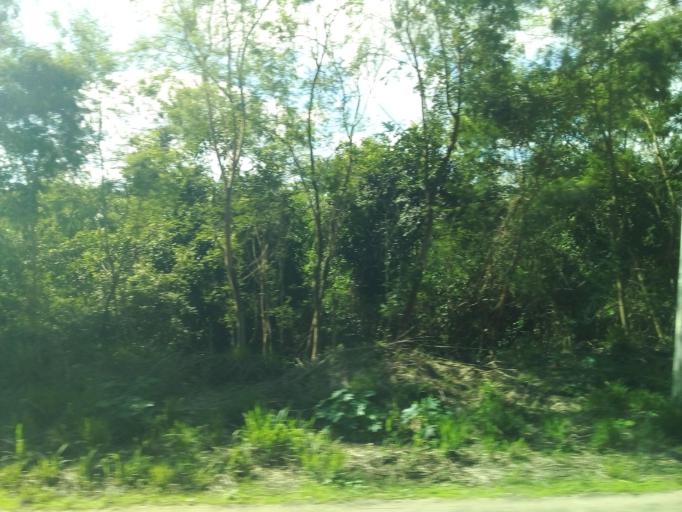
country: BR
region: Minas Gerais
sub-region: Governador Valadares
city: Governador Valadares
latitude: -18.8732
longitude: -41.7812
